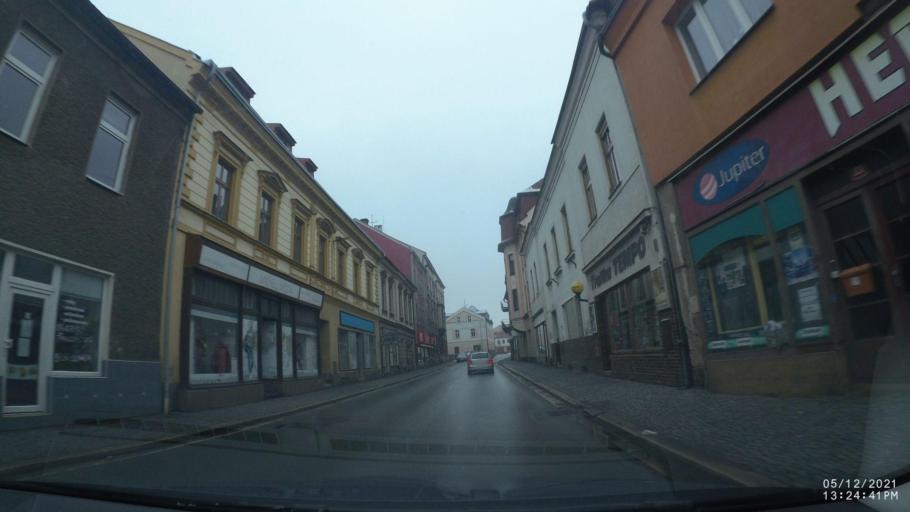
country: CZ
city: Hronov
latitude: 50.4786
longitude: 16.1816
